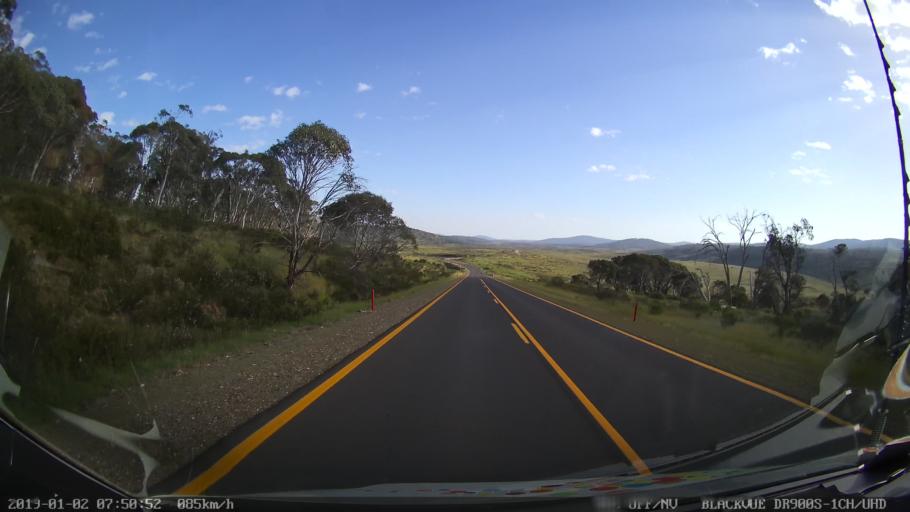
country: AU
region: New South Wales
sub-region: Tumut Shire
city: Tumut
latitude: -35.7254
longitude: 148.5294
